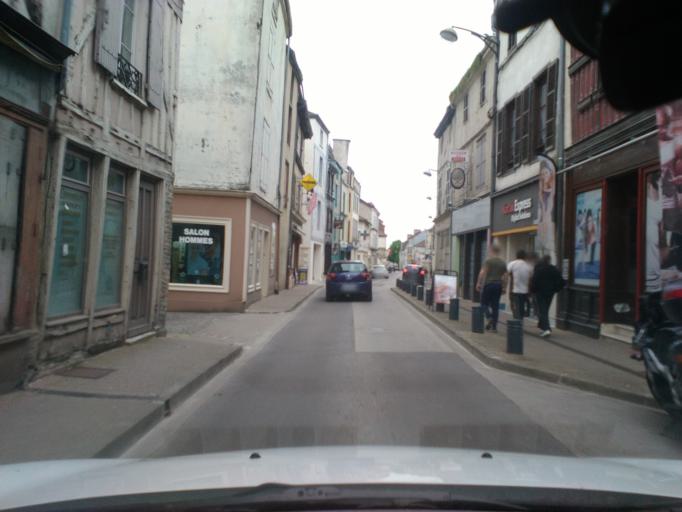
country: FR
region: Champagne-Ardenne
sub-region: Departement de l'Aube
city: Bar-sur-Aube
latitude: 48.2328
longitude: 4.7073
